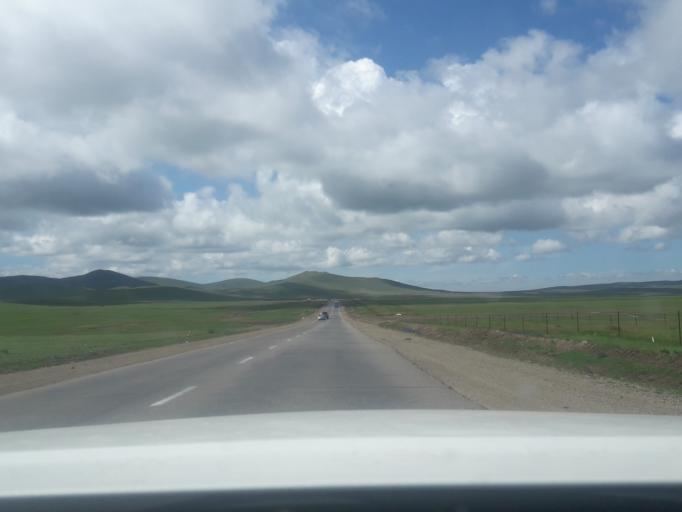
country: MN
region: Central Aimak
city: Altanbulag
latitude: 47.9004
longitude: 106.4606
